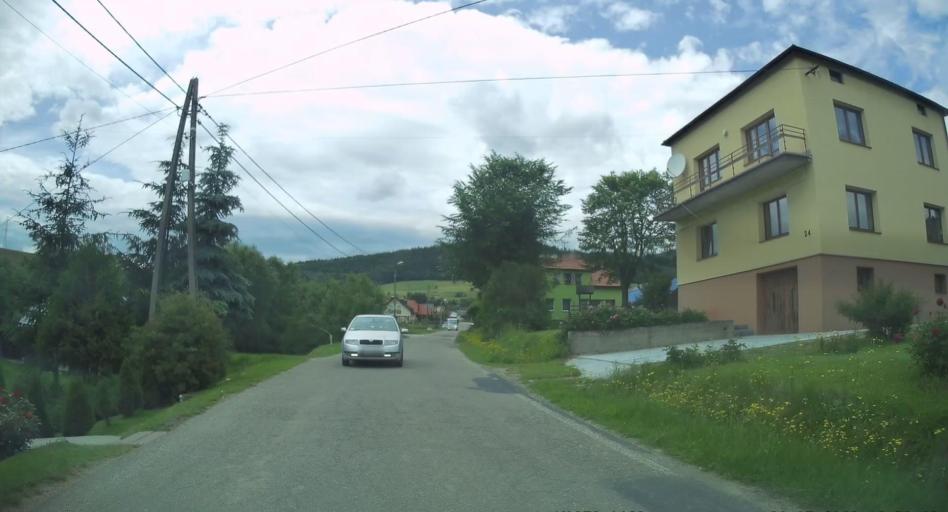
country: PL
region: Lesser Poland Voivodeship
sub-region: Powiat nowosadecki
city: Muszyna
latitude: 49.3873
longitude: 20.9127
